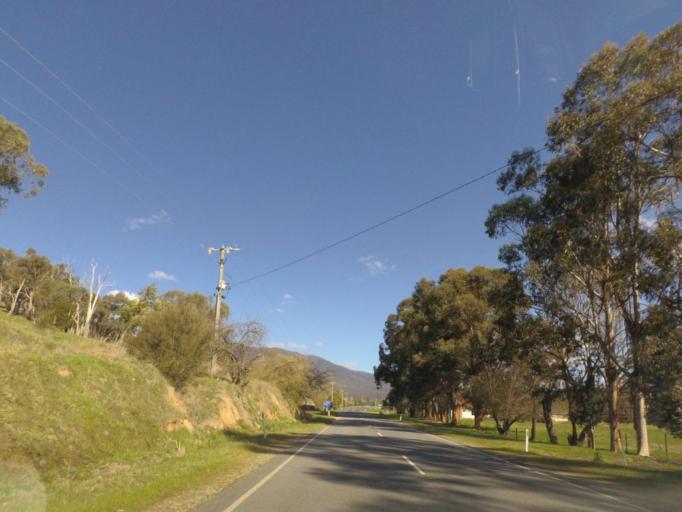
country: AU
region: Victoria
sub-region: Murrindindi
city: Alexandra
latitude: -37.2765
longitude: 145.7997
